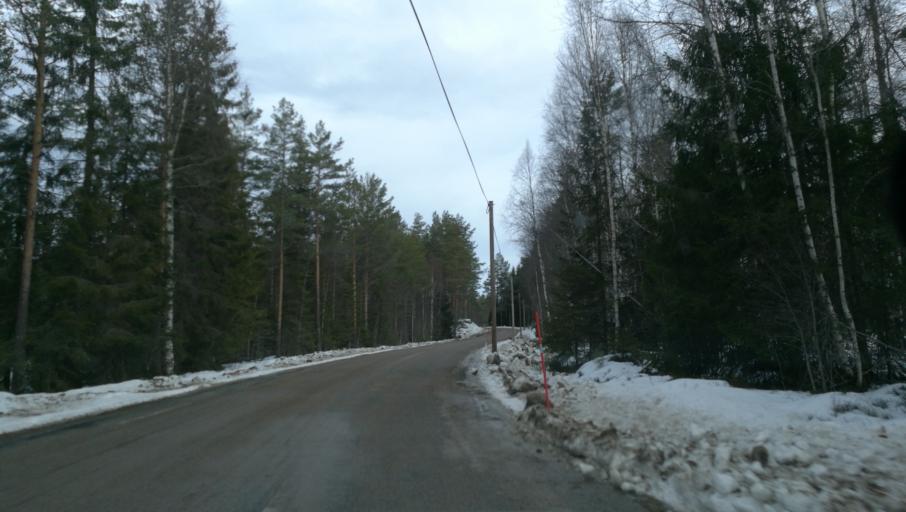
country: NO
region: Hedmark
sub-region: Grue
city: Kirkenaer
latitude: 60.4993
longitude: 12.5593
